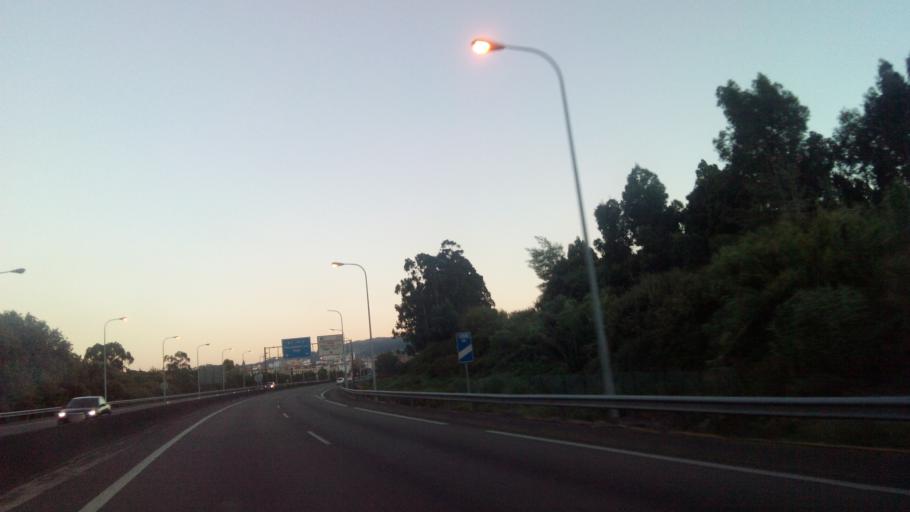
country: ES
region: Galicia
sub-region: Provincia de Pontevedra
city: Pontevedra
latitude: 42.4438
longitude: -8.6481
